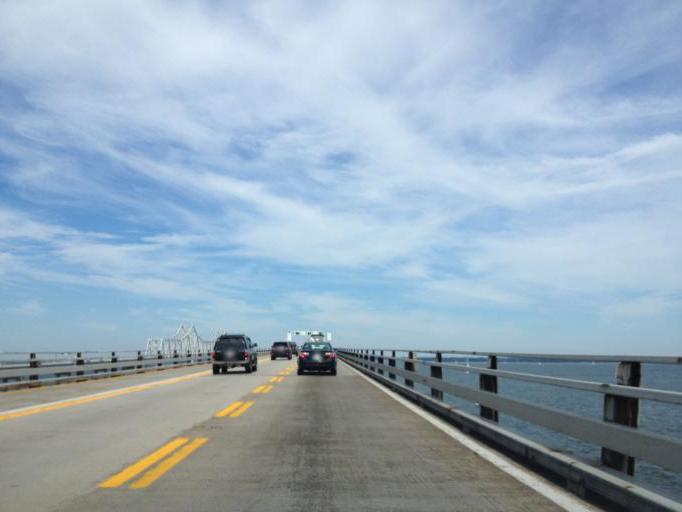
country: US
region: Maryland
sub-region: Queen Anne's County
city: Stevensville
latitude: 38.9868
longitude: -76.3491
